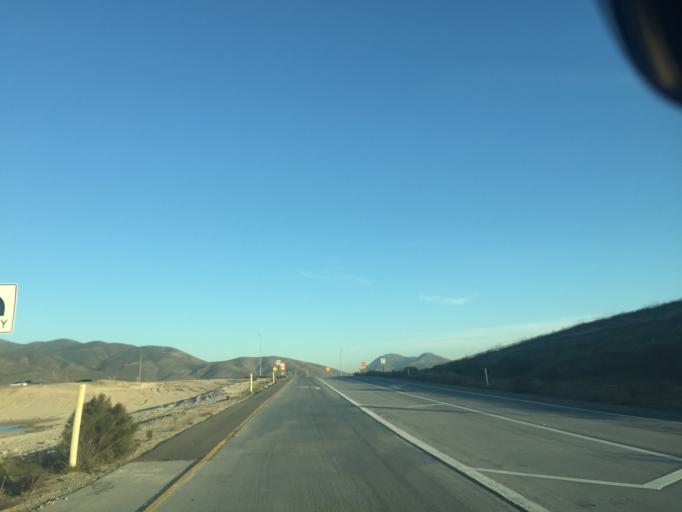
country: MX
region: Baja California
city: Tijuana
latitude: 32.5636
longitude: -116.9299
